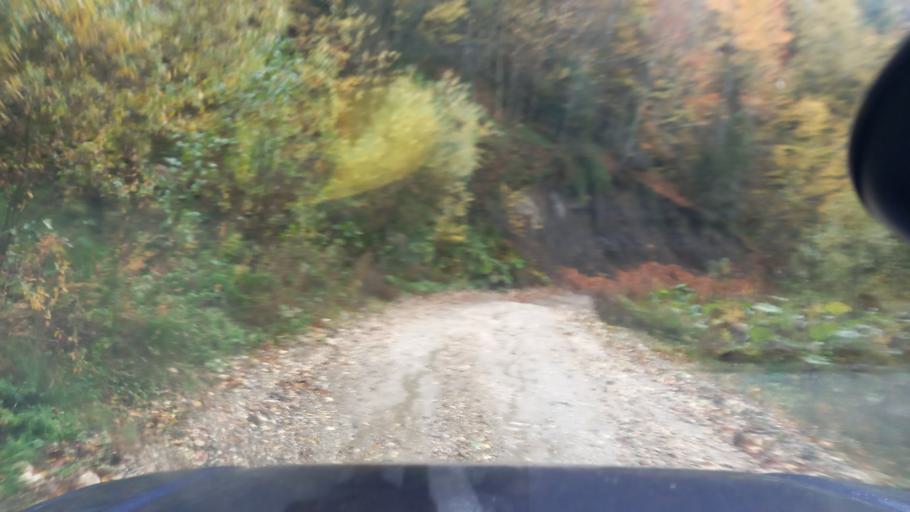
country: RU
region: Krasnodarskiy
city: Neftegorsk
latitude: 44.0343
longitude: 39.8370
